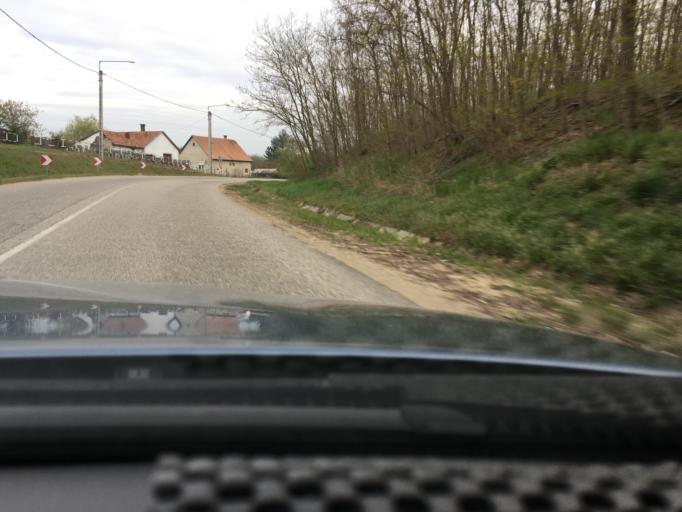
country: HU
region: Hajdu-Bihar
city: Hajdusamson
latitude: 47.5753
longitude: 21.7699
